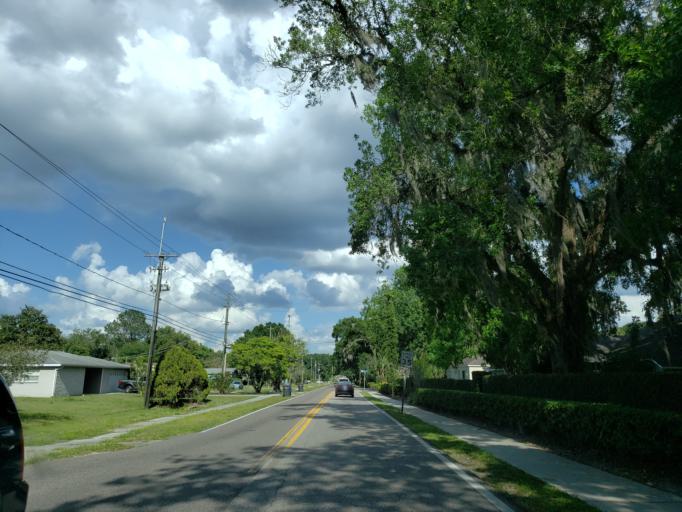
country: US
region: Florida
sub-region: Hillsborough County
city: Mango
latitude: 27.9597
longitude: -82.2981
